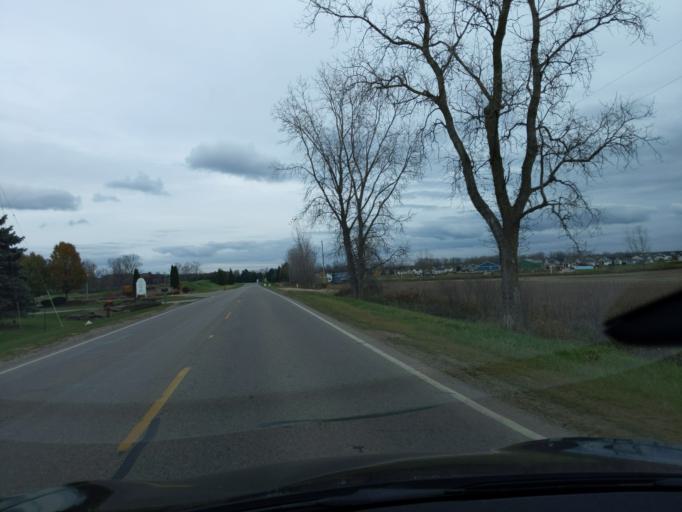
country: US
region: Michigan
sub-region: Ingham County
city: East Lansing
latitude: 42.7841
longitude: -84.4996
